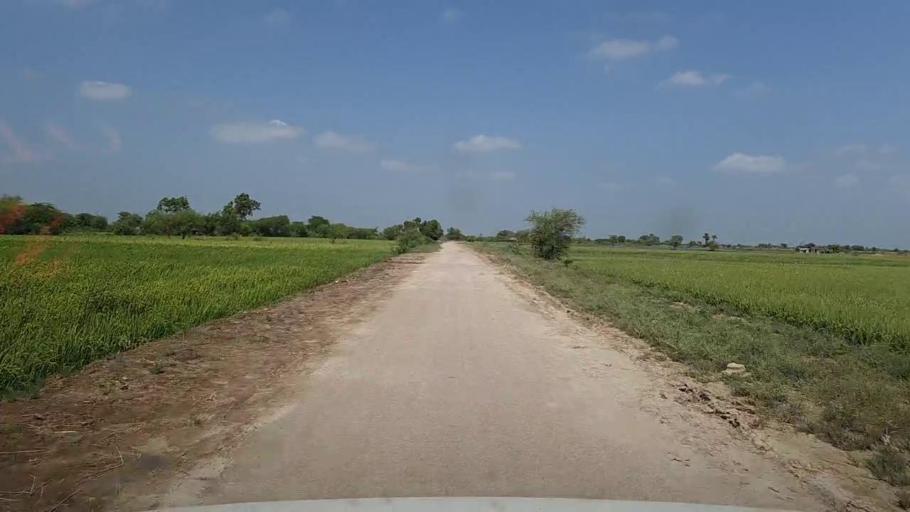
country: PK
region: Sindh
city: Kario
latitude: 24.6908
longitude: 68.5880
